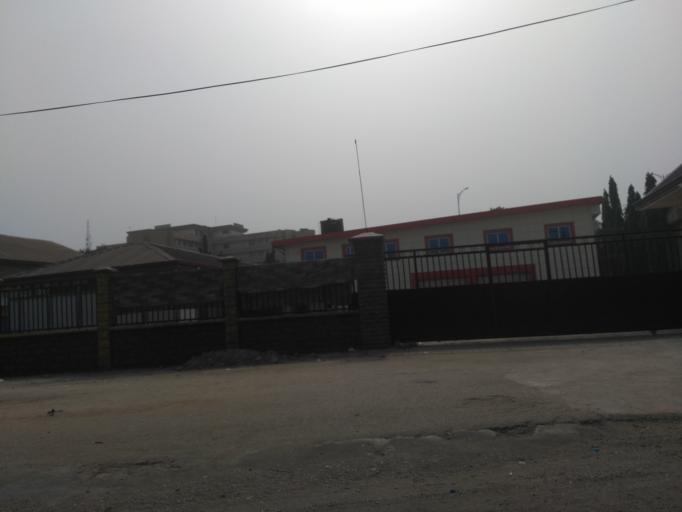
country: GH
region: Ashanti
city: Kumasi
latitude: 6.6891
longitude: -1.6171
